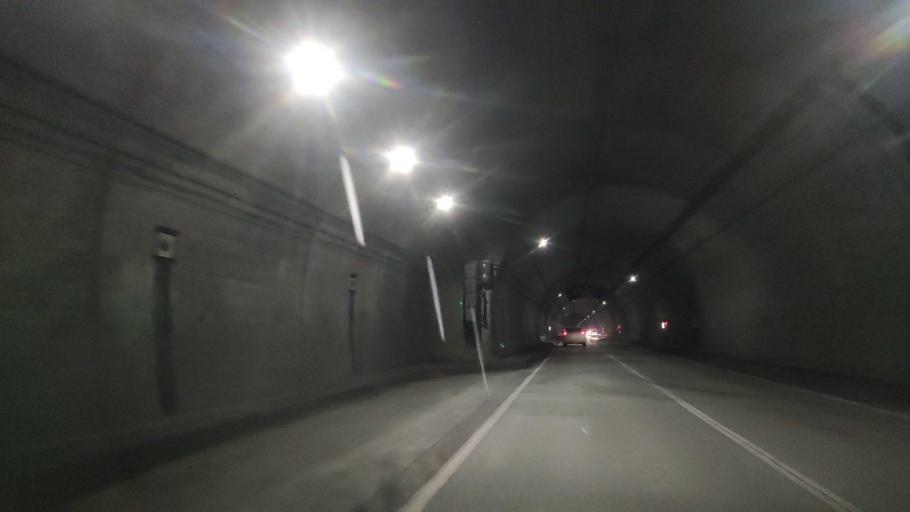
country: JP
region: Hokkaido
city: Rumoi
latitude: 43.7204
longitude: 141.3300
